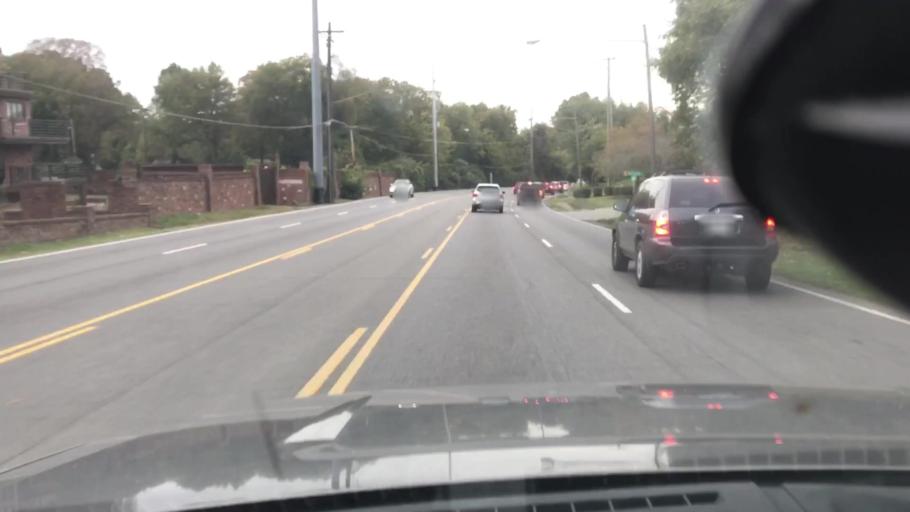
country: US
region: Tennessee
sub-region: Davidson County
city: Oak Hill
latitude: 36.1161
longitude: -86.8105
